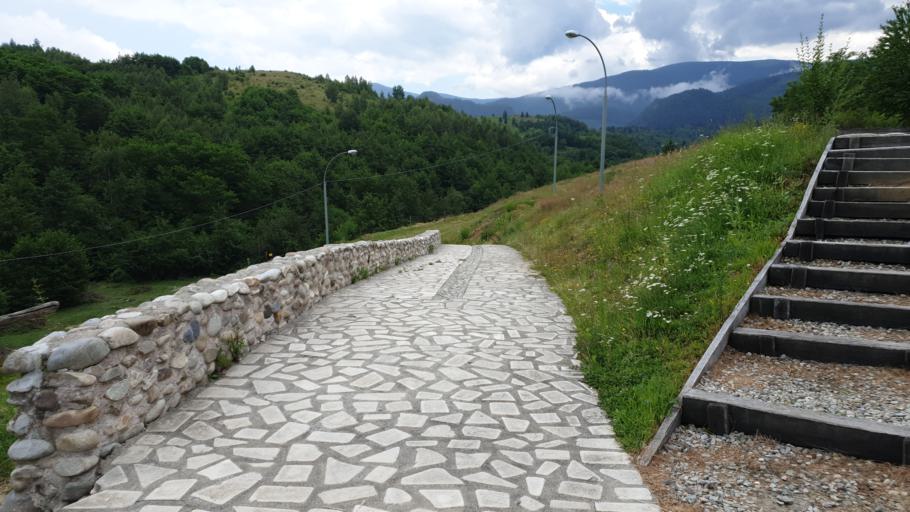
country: RO
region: Hunedoara
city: Salasu de Sus
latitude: 45.4830
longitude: 22.9474
